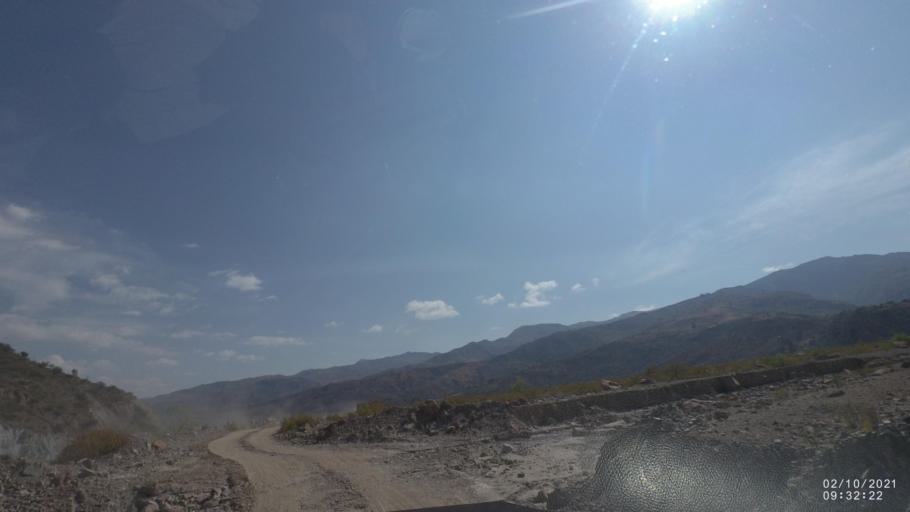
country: BO
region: Cochabamba
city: Irpa Irpa
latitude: -17.8464
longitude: -66.3207
